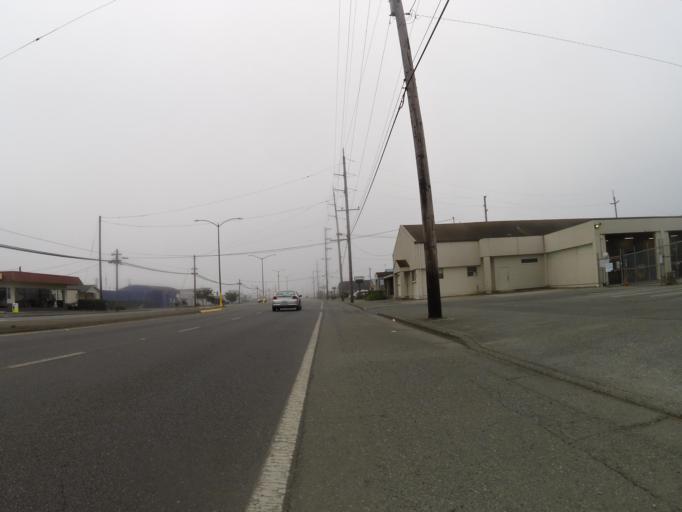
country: US
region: California
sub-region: Del Norte County
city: Crescent City
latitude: 41.7669
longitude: -124.1987
